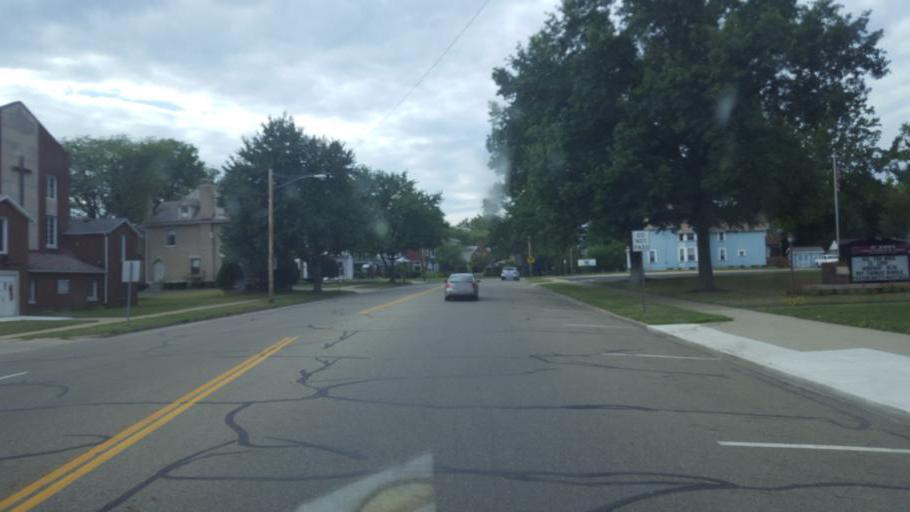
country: US
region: Ohio
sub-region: Tuscarawas County
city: Dover
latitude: 40.5238
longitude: -81.4781
